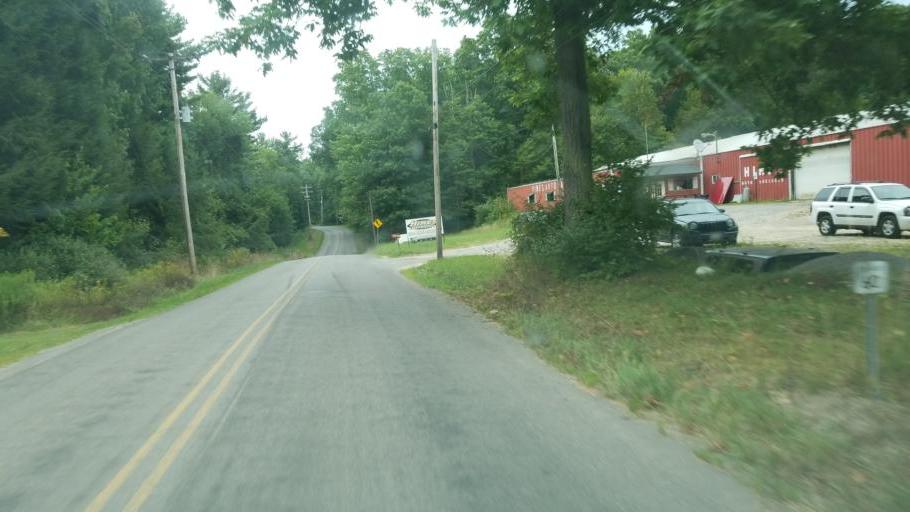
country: US
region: Pennsylvania
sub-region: Clarion County
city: Marianne
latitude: 41.1992
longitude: -79.4497
